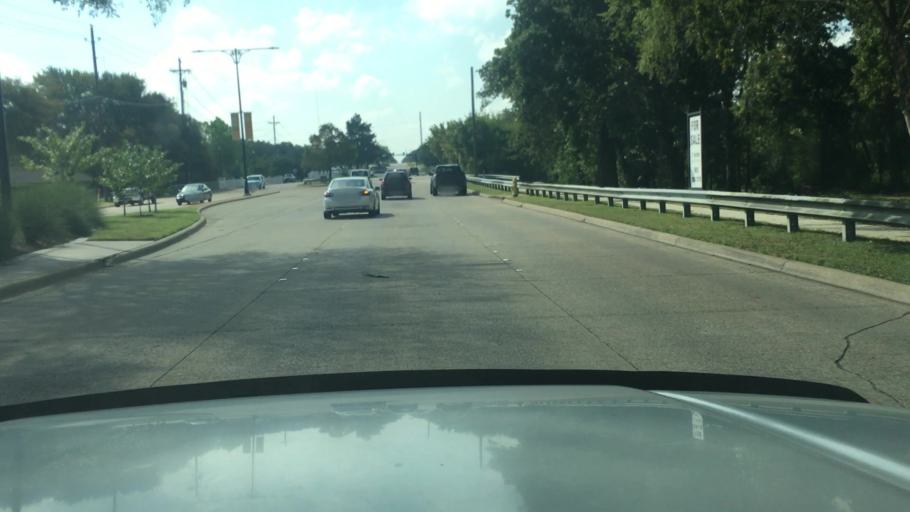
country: US
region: Texas
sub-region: Dallas County
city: Coppell
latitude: 32.9571
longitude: -96.9936
